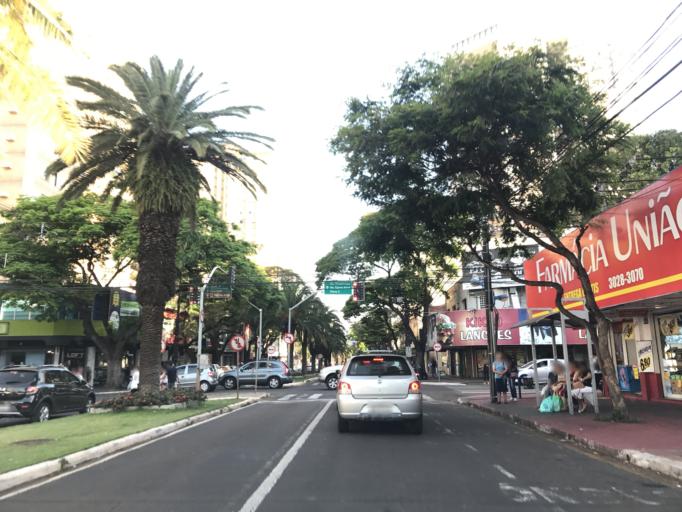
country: BR
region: Parana
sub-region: Maringa
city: Maringa
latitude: -23.4224
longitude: -51.9365
